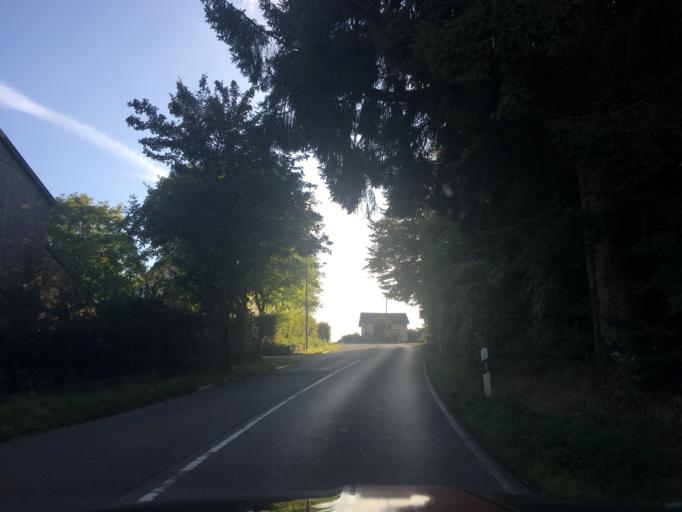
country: FR
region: Lorraine
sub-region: Departement de Meurthe-et-Moselle
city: Hussigny-Godbrange
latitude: 49.5099
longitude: 5.8722
